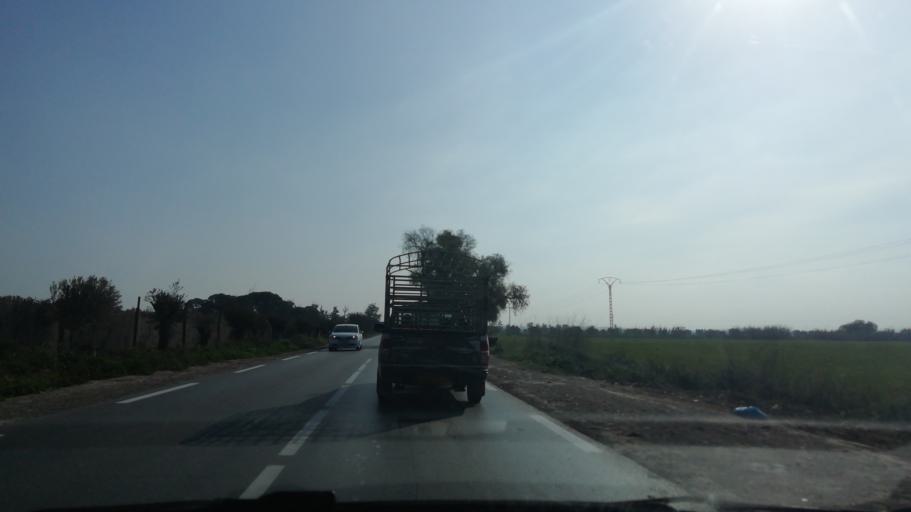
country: DZ
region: Mostaganem
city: Mostaganem
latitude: 35.7424
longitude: -0.0076
